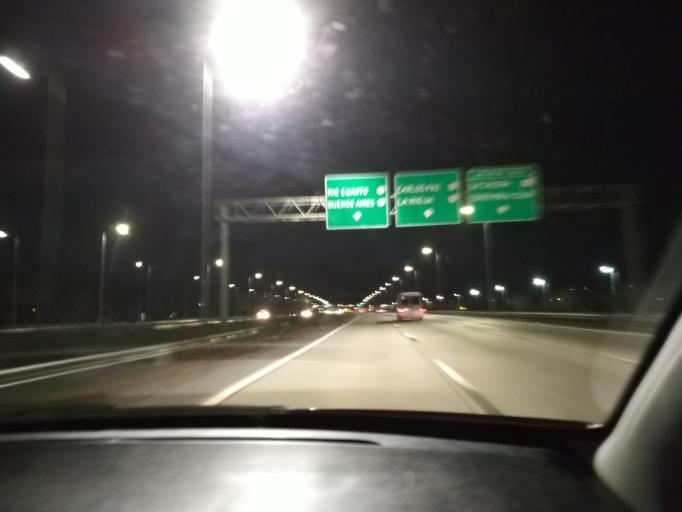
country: AR
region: Cordoba
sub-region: Departamento de Capital
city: Cordoba
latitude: -31.3817
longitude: -64.2592
